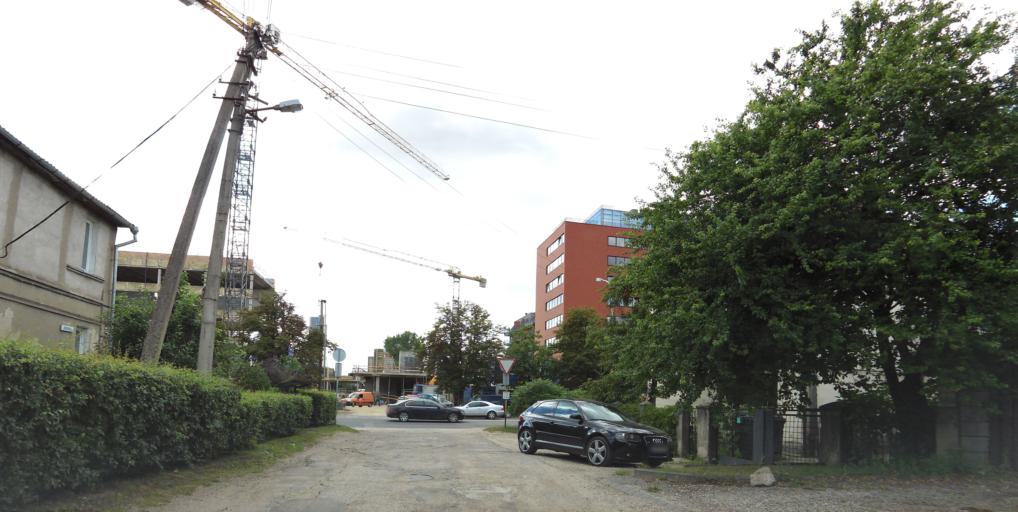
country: LT
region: Vilnius County
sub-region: Vilnius
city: Vilnius
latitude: 54.7045
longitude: 25.2778
